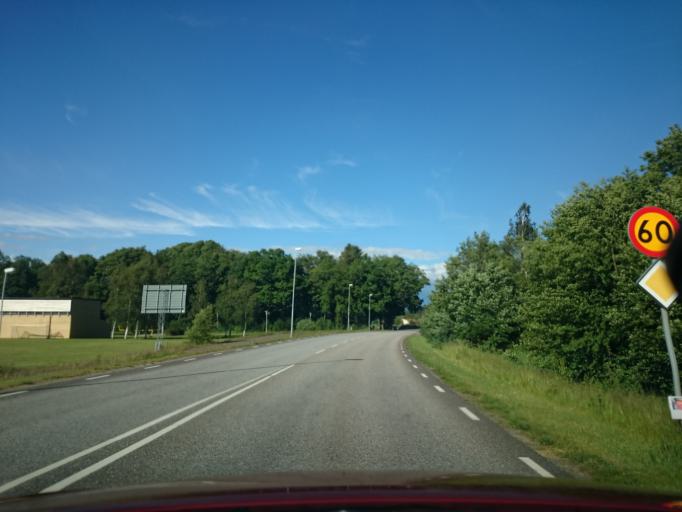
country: SE
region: Vaestra Goetaland
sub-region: Lerums Kommun
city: Stenkullen
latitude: 57.7829
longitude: 12.2979
